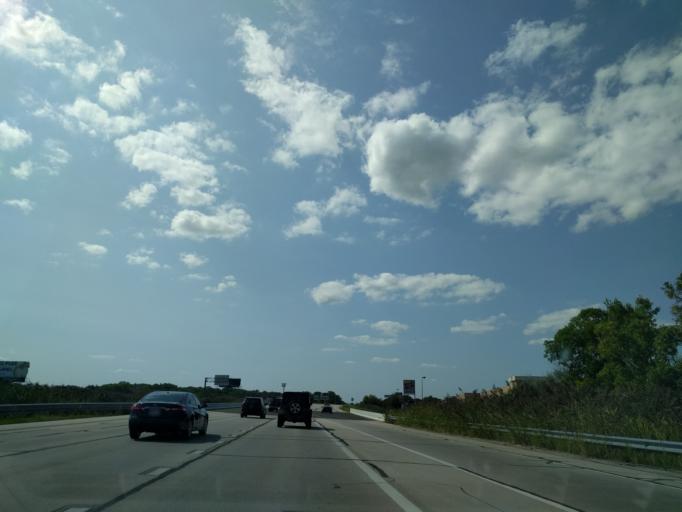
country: US
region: Wisconsin
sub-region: Brown County
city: Ashwaubenon
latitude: 44.4794
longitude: -88.0656
